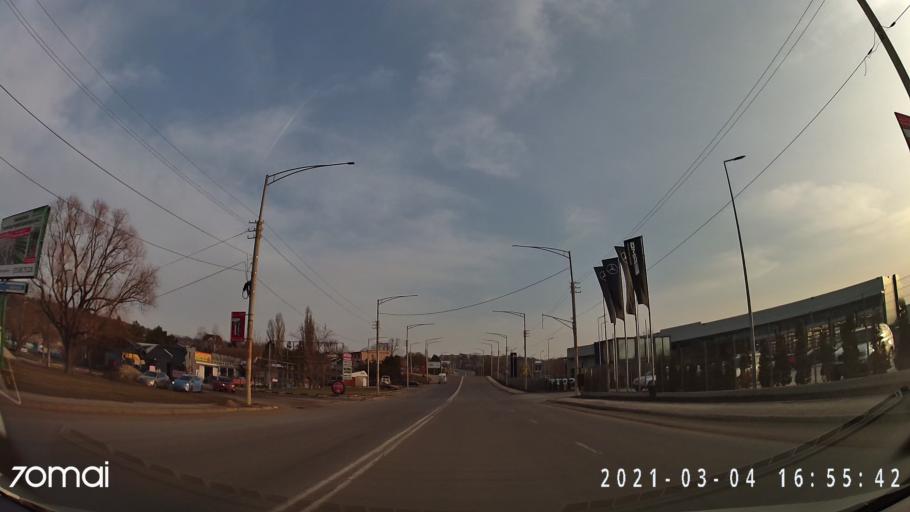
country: MD
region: Balti
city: Balti
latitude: 47.7543
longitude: 27.9422
